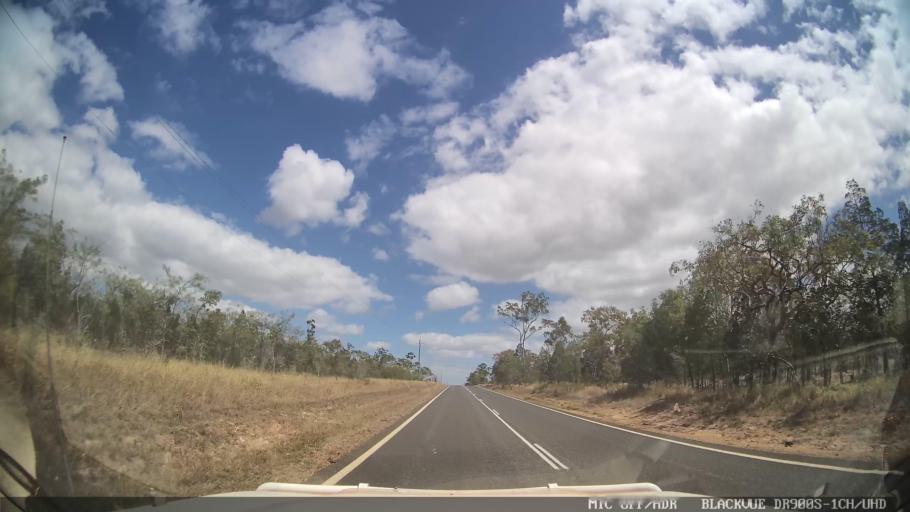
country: AU
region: Queensland
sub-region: Tablelands
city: Ravenshoe
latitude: -17.7291
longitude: 145.0456
